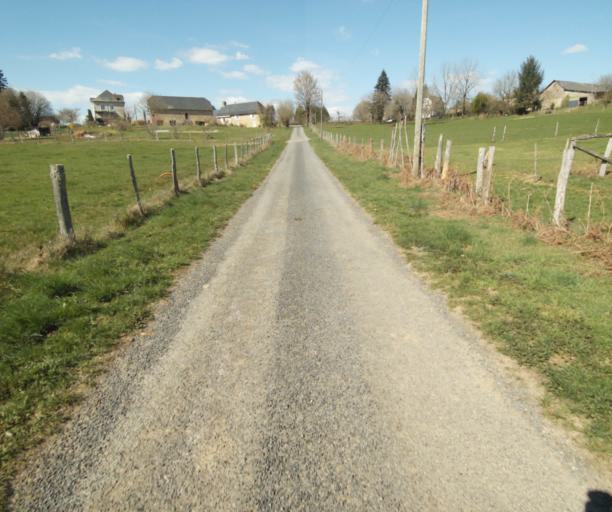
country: FR
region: Limousin
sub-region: Departement de la Correze
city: Saint-Mexant
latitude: 45.2896
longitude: 1.6827
